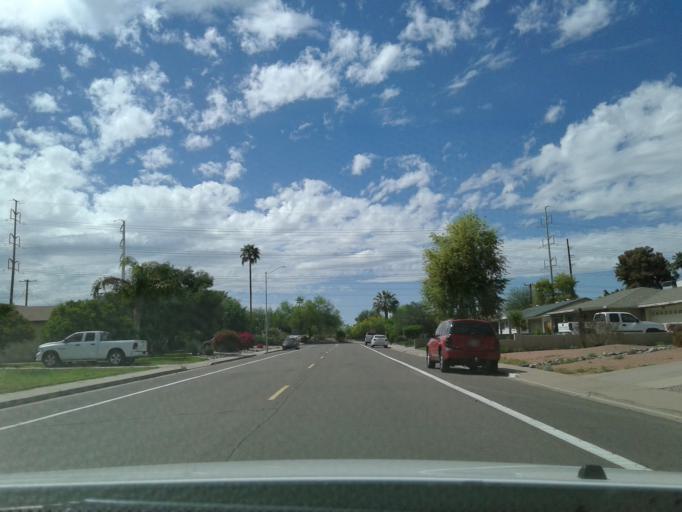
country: US
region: Arizona
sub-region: Maricopa County
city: Scottsdale
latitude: 33.4730
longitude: -111.9369
